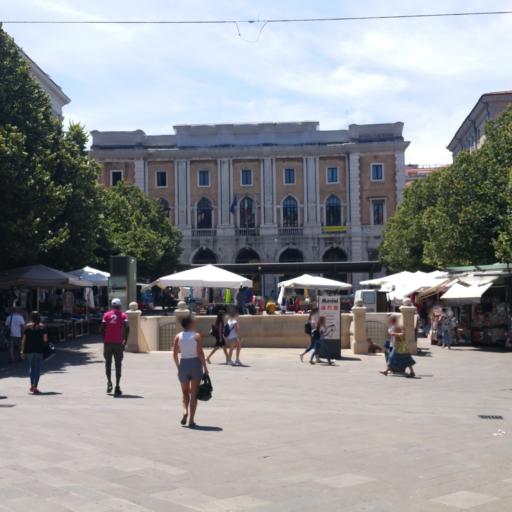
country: IT
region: The Marches
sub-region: Provincia di Ancona
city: Le Grazie di Ancona
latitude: 43.6179
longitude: 13.5132
